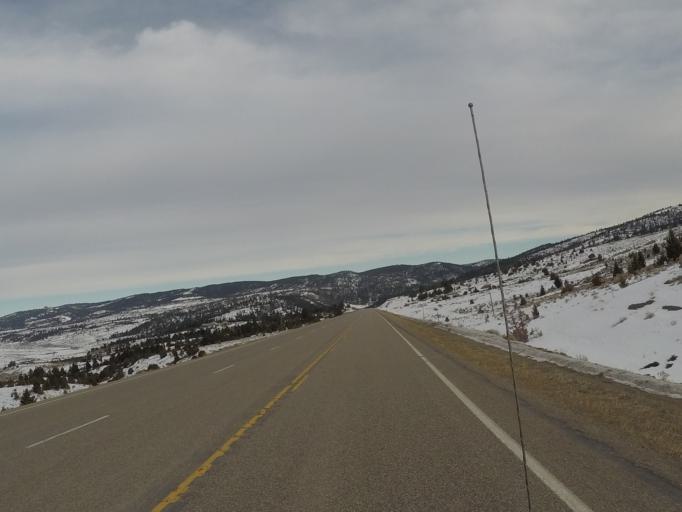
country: US
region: Montana
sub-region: Meagher County
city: White Sulphur Springs
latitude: 46.6521
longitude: -110.8712
